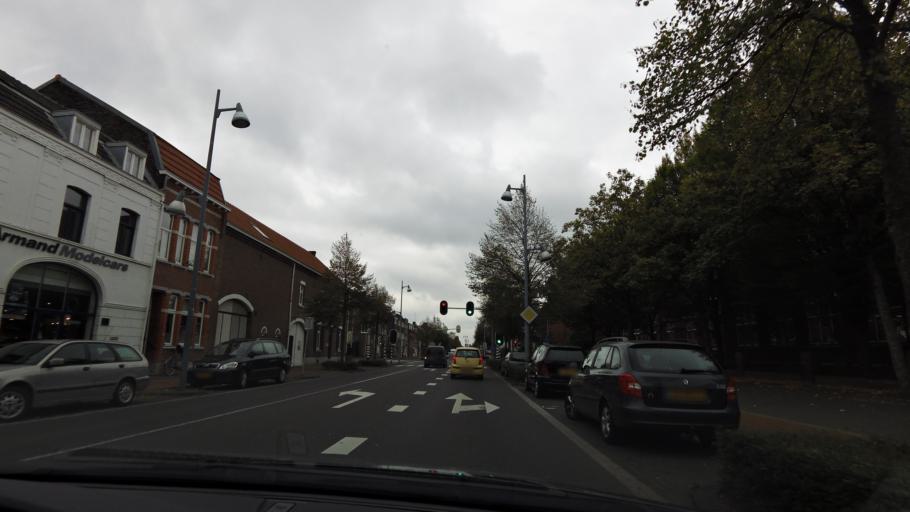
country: NL
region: Limburg
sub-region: Gemeente Sittard-Geleen
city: Sittard
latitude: 50.9951
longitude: 5.8589
